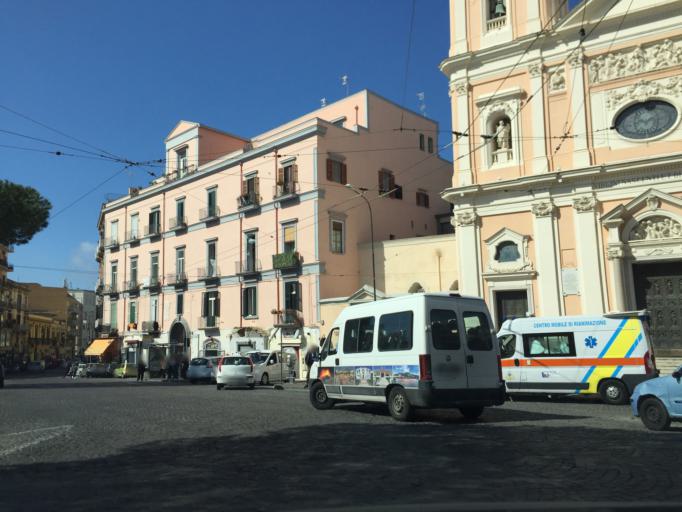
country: IT
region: Campania
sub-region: Provincia di Napoli
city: Portici
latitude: 40.8142
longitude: 14.3393
